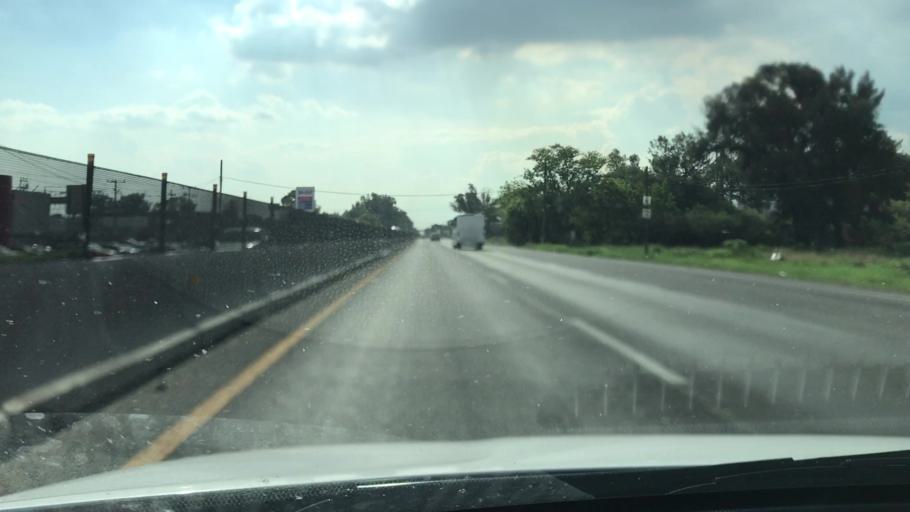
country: MX
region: Guanajuato
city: Valtierrilla
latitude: 20.5499
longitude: -101.1418
